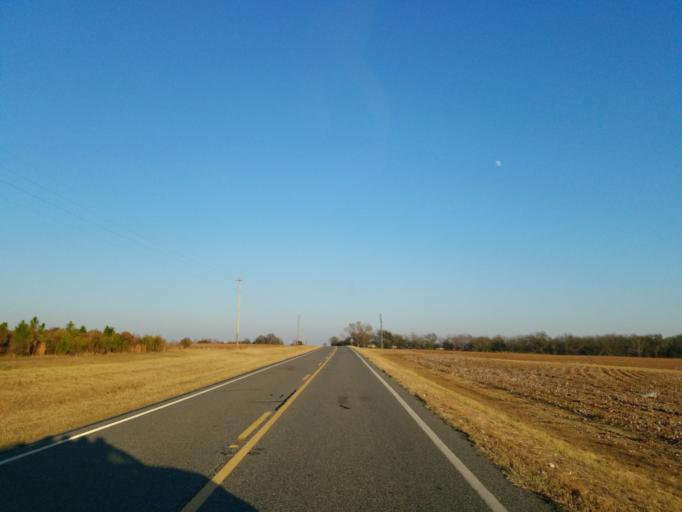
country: US
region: Georgia
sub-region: Turner County
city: Ashburn
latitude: 31.8596
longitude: -83.6073
